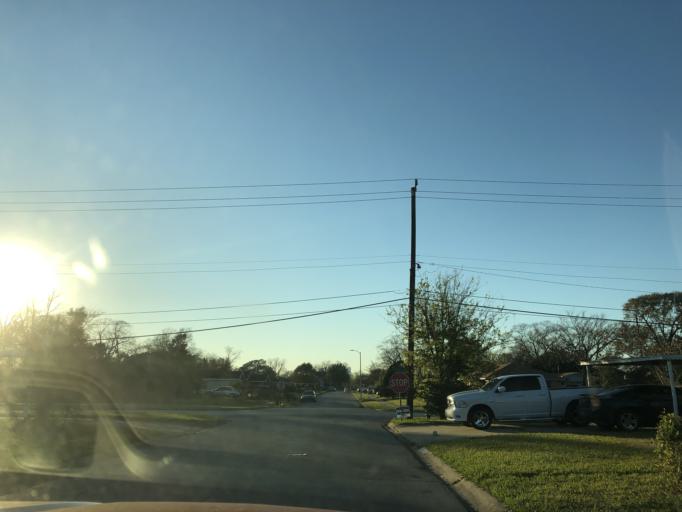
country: US
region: Texas
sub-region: Harris County
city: Jacinto City
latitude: 29.7609
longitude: -95.2708
